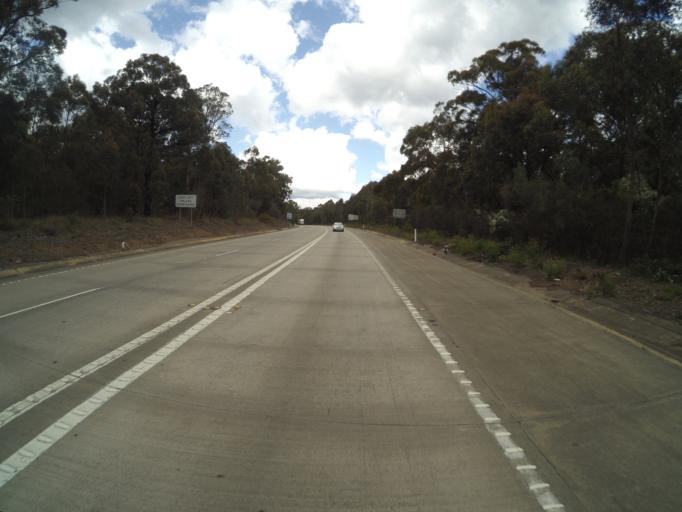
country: AU
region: New South Wales
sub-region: Wollondilly
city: Douglas Park
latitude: -34.2694
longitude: 150.7137
